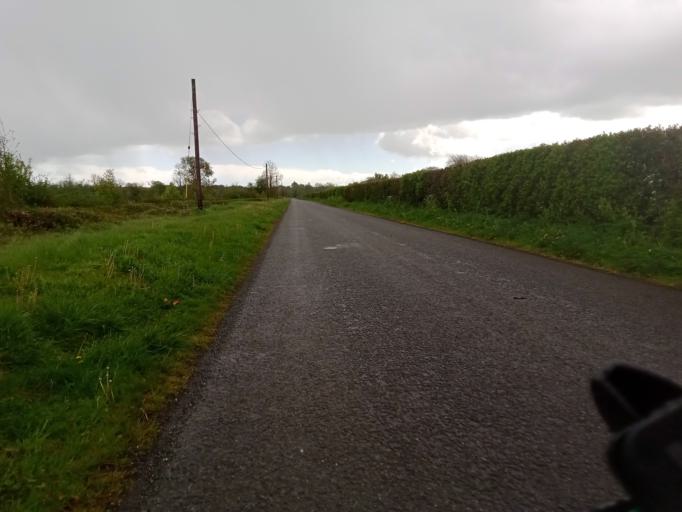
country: IE
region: Leinster
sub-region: Kilkenny
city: Kilkenny
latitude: 52.6798
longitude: -7.2656
